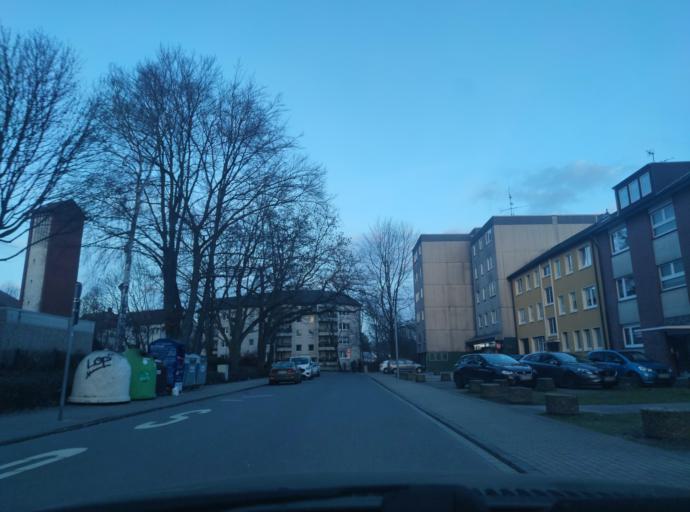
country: DE
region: North Rhine-Westphalia
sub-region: Regierungsbezirk Munster
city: Gelsenkirchen
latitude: 51.4903
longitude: 7.0917
